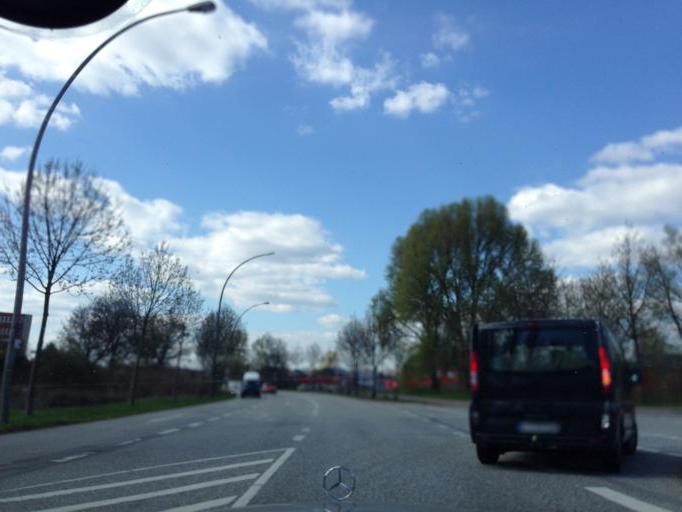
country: DE
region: Hamburg
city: Wandsbek
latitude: 53.5299
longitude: 10.1082
